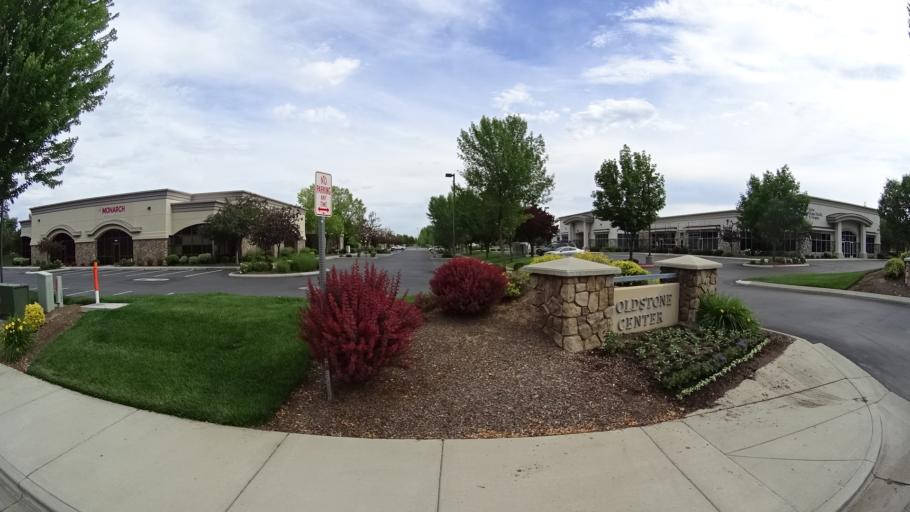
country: US
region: Idaho
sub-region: Ada County
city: Meridian
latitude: 43.5855
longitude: -116.3530
